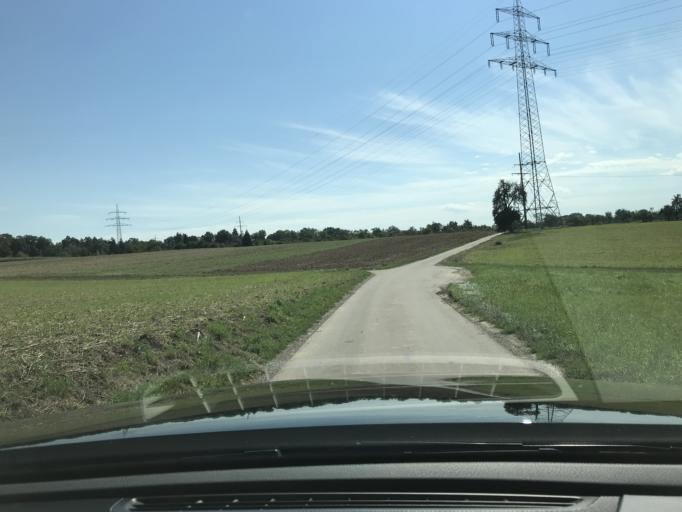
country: DE
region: Baden-Wuerttemberg
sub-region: Regierungsbezirk Stuttgart
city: Affalterbach
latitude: 48.9029
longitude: 9.3134
